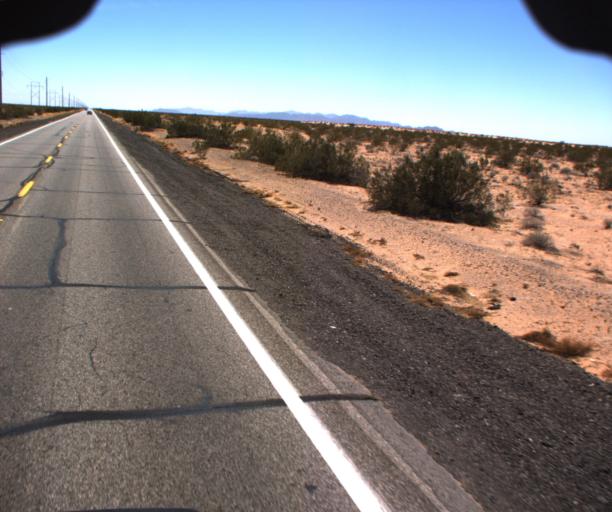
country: US
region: Arizona
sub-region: La Paz County
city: Quartzsite
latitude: 33.9104
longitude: -114.2169
